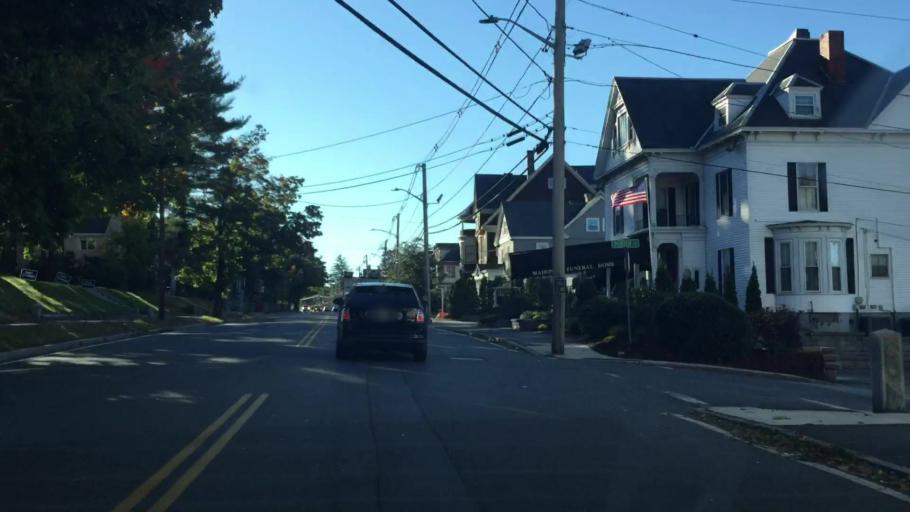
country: US
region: Massachusetts
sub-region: Middlesex County
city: Lowell
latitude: 42.6414
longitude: -71.2970
